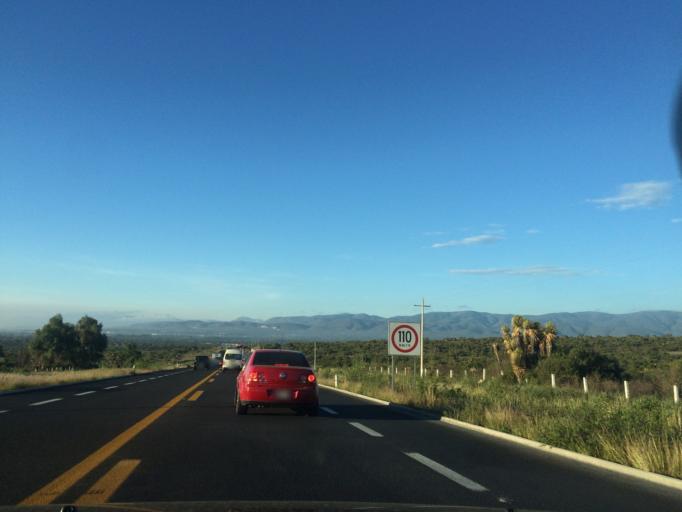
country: MX
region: Puebla
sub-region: Tehuacan
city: Magdalena Cuayucatepec
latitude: 18.5685
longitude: -97.4640
